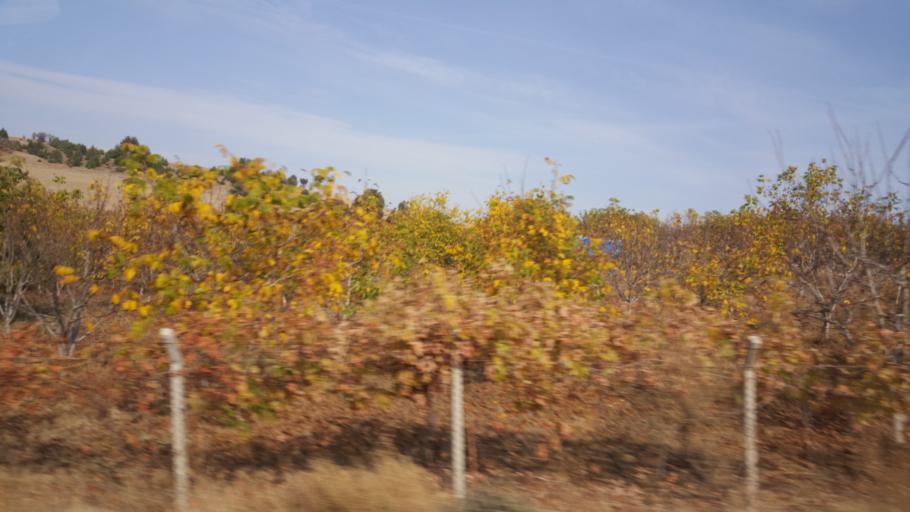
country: TR
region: Eskisehir
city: Mihaliccik
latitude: 39.9621
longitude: 31.3908
